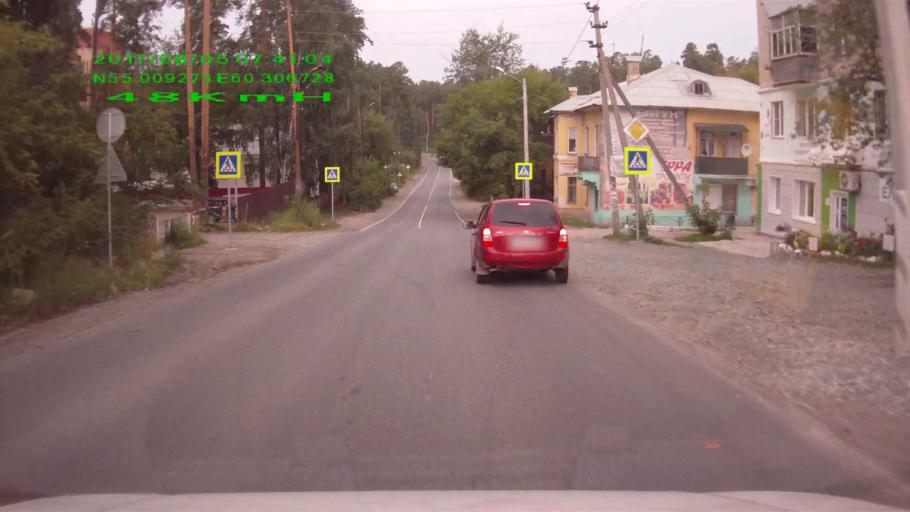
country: RU
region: Chelyabinsk
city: Chebarkul'
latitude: 55.0094
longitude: 60.3064
